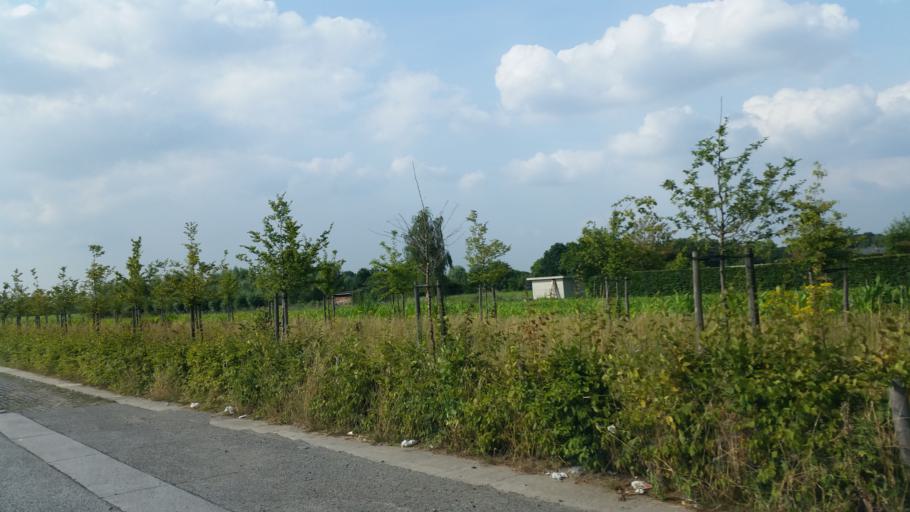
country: BE
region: Flanders
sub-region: Provincie Vlaams-Brabant
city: Boortmeerbeek
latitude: 50.9621
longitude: 4.5922
